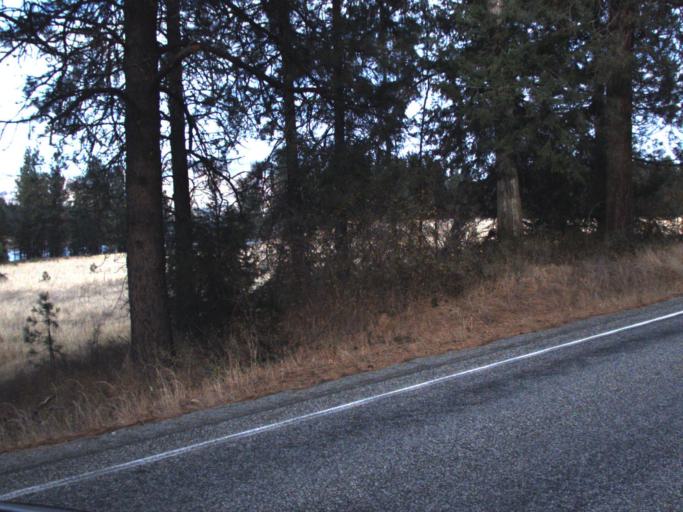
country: US
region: Washington
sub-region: Stevens County
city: Kettle Falls
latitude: 48.8104
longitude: -117.9432
